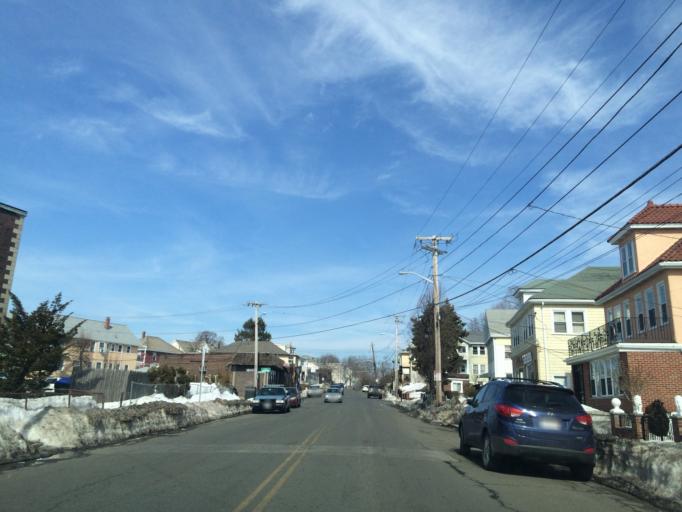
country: US
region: Massachusetts
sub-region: Middlesex County
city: Medford
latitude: 42.4087
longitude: -71.1094
